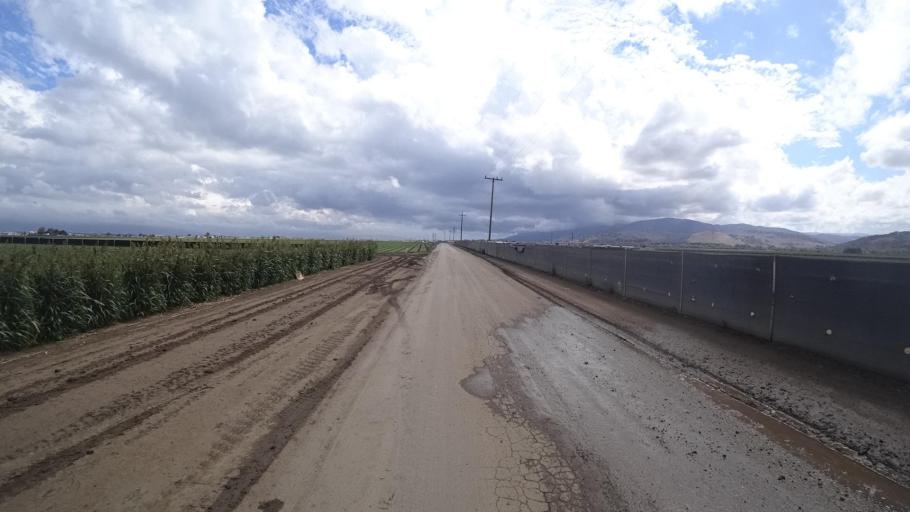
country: US
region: California
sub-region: Monterey County
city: Salinas
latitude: 36.6468
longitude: -121.6872
